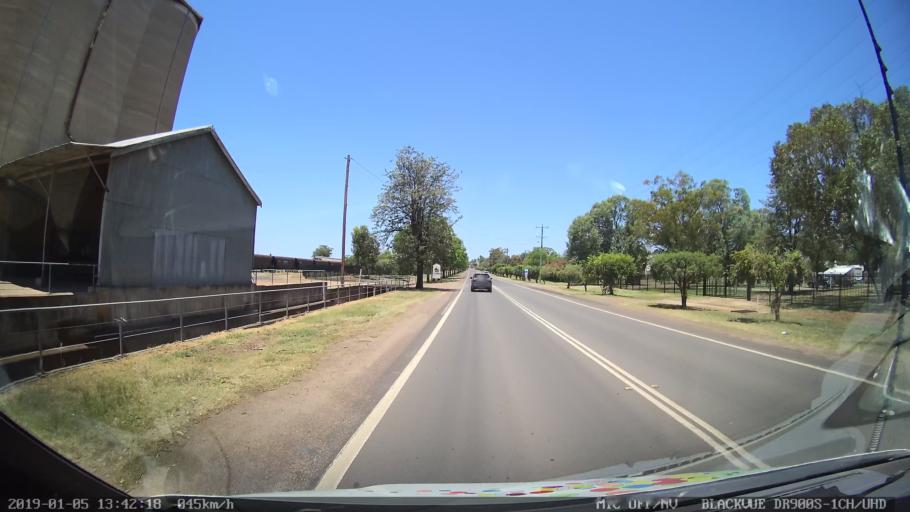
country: AU
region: New South Wales
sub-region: Gunnedah
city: Gunnedah
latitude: -30.9779
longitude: 150.2442
